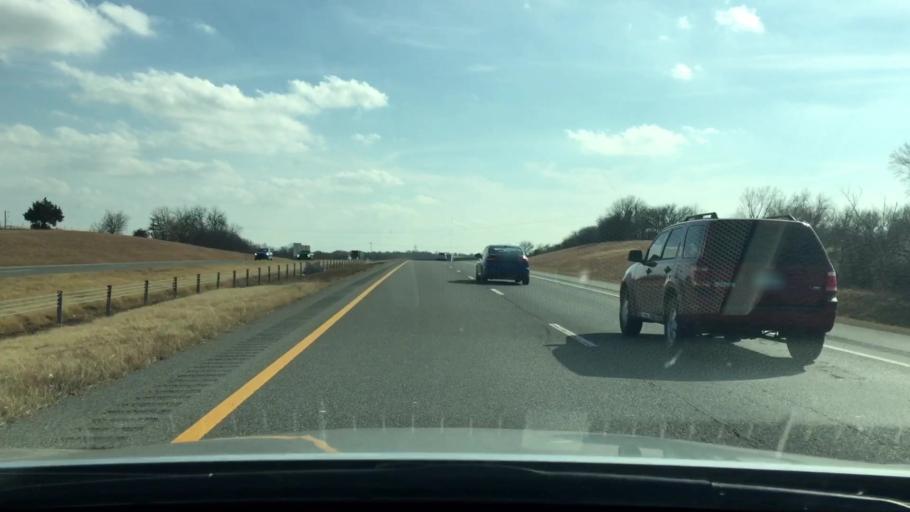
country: US
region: Oklahoma
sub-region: McClain County
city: Purcell
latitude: 34.9627
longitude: -97.3697
